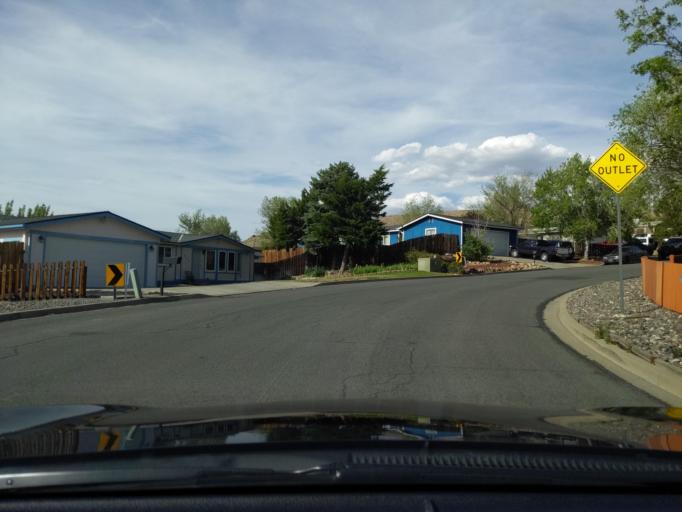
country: US
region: Nevada
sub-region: Washoe County
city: Sun Valley
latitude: 39.5806
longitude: -119.7702
